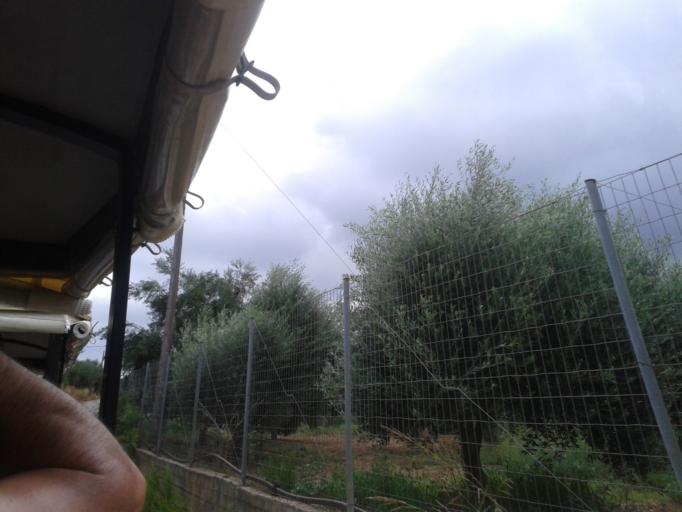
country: GR
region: Crete
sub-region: Nomos Chanias
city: Perivolia
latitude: 35.4862
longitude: 23.9819
